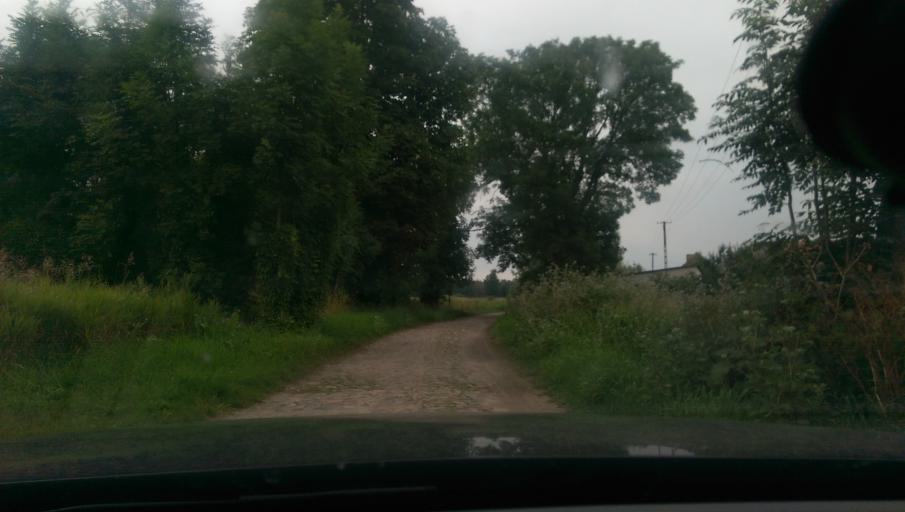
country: PL
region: Warmian-Masurian Voivodeship
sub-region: Powiat piski
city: Orzysz
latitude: 53.8152
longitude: 21.8016
